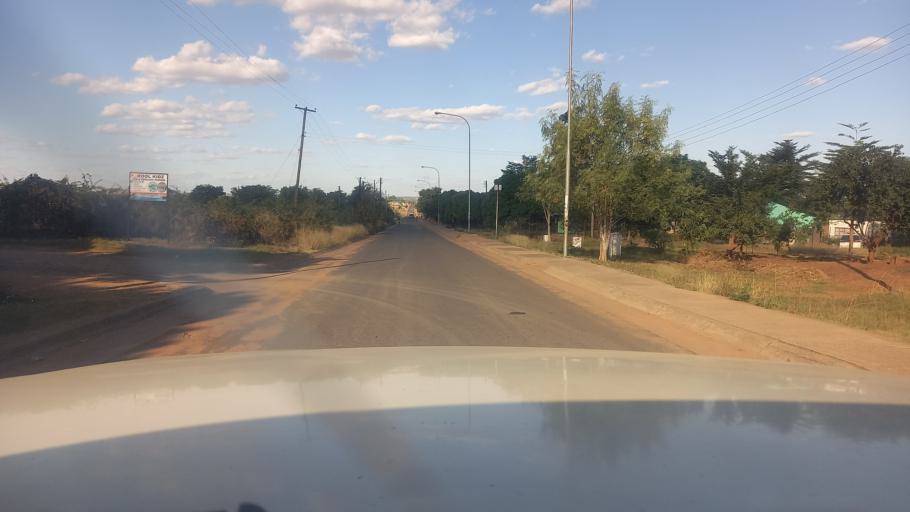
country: ZM
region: Southern
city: Livingstone
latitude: -17.8303
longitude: 25.8674
